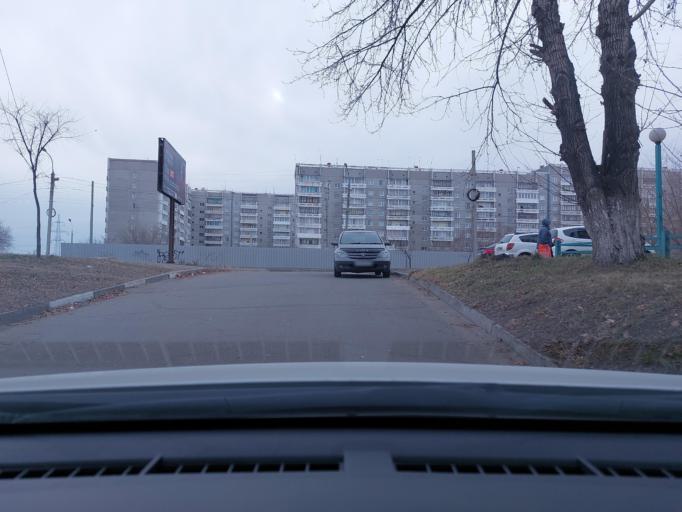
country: RU
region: Irkutsk
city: Smolenshchina
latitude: 52.3482
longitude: 104.1655
